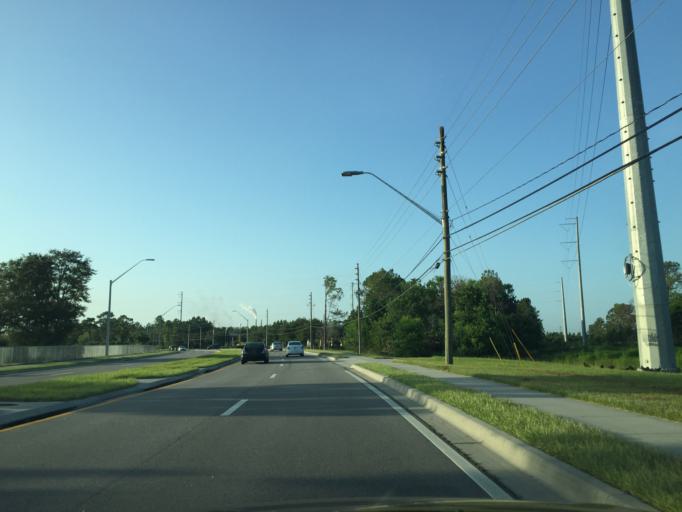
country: US
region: Florida
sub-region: Orange County
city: Alafaya
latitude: 28.5142
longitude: -81.1863
